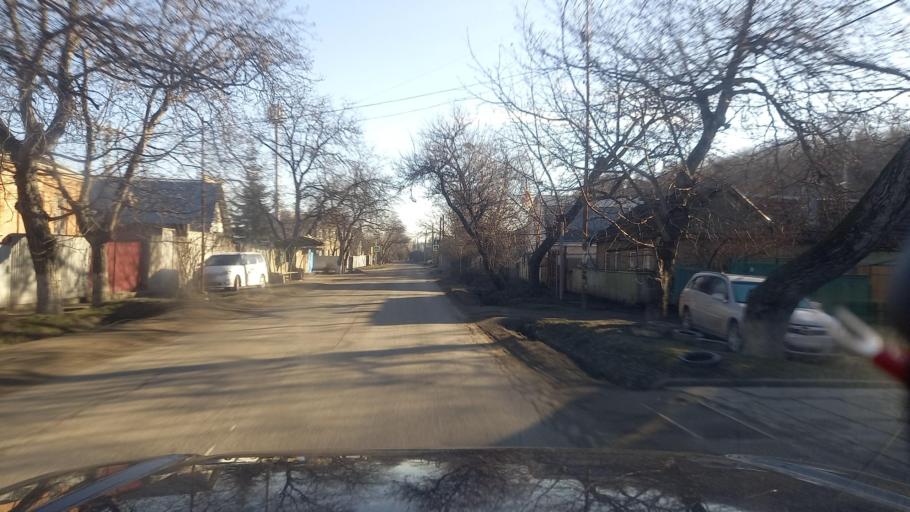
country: RU
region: Stavropol'skiy
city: Svobody
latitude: 44.0238
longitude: 43.0580
